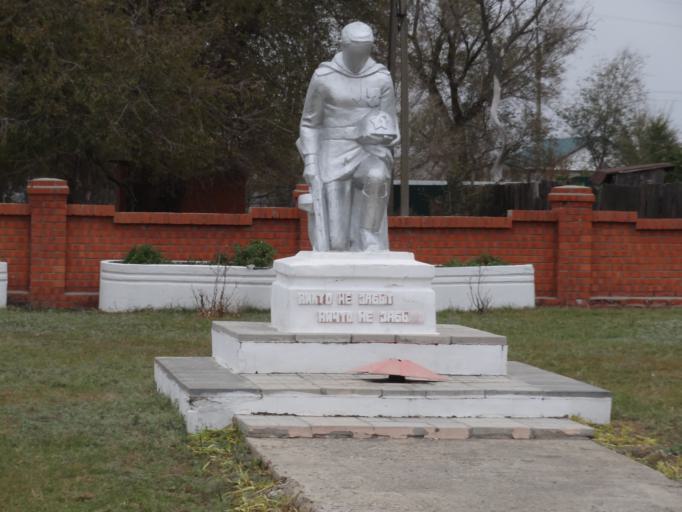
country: RU
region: Saratov
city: Sovetskoye
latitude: 51.5303
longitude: 46.6111
